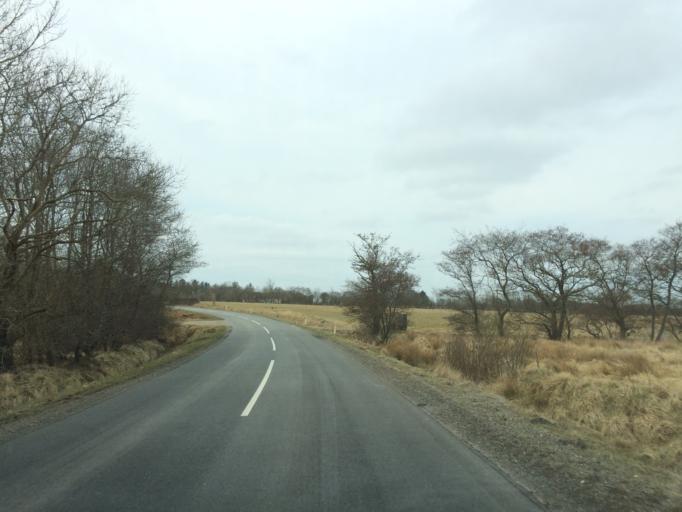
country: DK
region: South Denmark
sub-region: Varde Kommune
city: Oksbol
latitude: 55.7928
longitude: 8.3482
